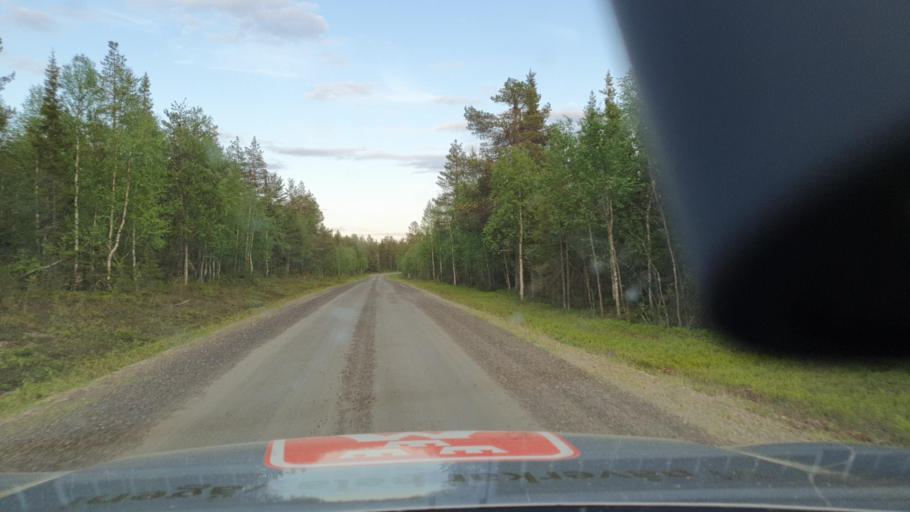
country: SE
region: Norrbotten
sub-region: Bodens Kommun
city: Boden
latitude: 66.5528
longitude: 21.4591
